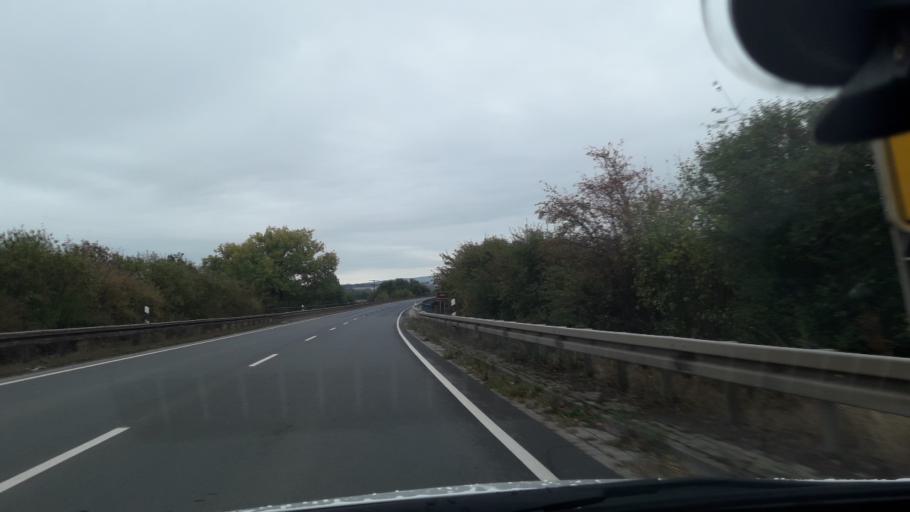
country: DE
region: Lower Saxony
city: Schladen
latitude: 52.0285
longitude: 10.5411
